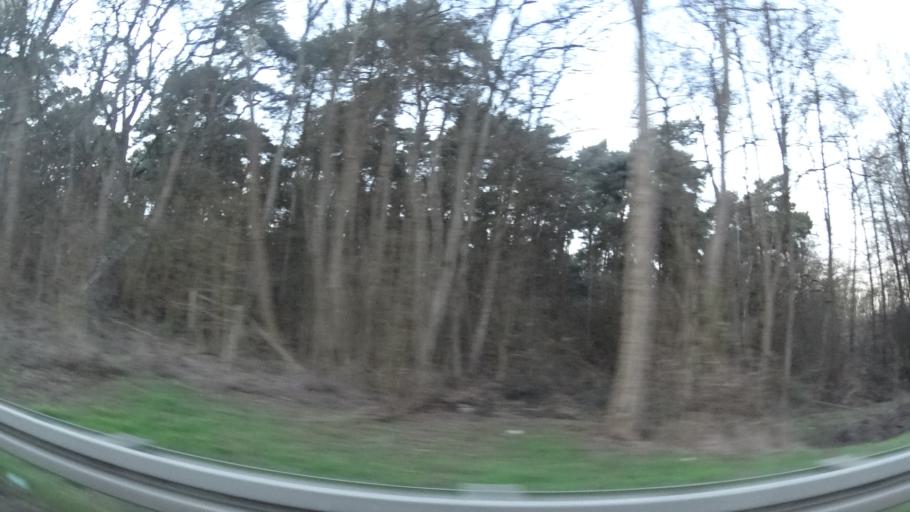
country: DE
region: Bavaria
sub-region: Regierungsbezirk Unterfranken
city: Alzenau in Unterfranken
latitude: 50.0986
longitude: 9.0812
